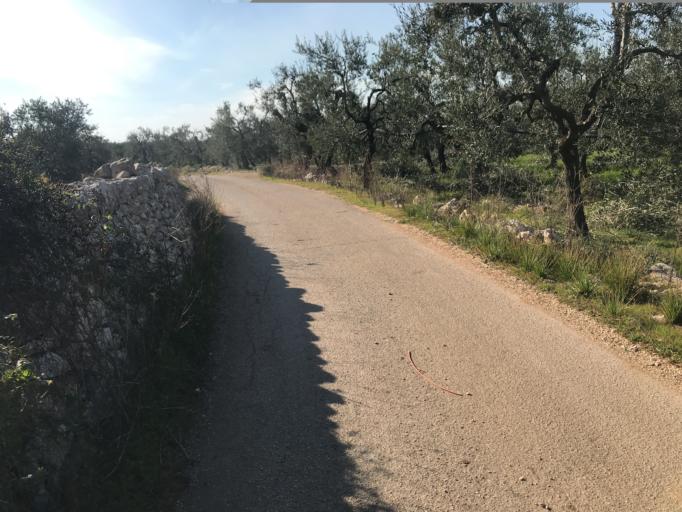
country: IT
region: Apulia
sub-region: Provincia di Bari
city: Corato
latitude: 41.1643
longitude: 16.4331
